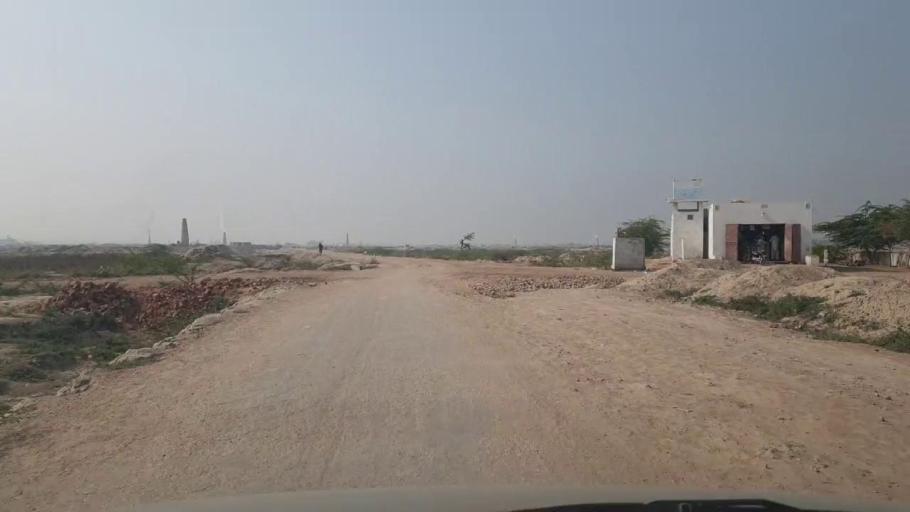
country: PK
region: Sindh
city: Umarkot
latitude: 25.3942
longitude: 69.7492
